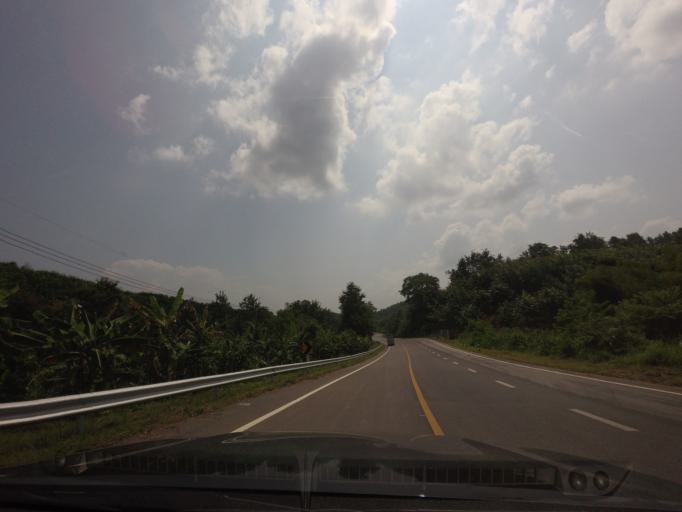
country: TH
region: Nan
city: Santi Suk
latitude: 18.9274
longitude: 100.8999
